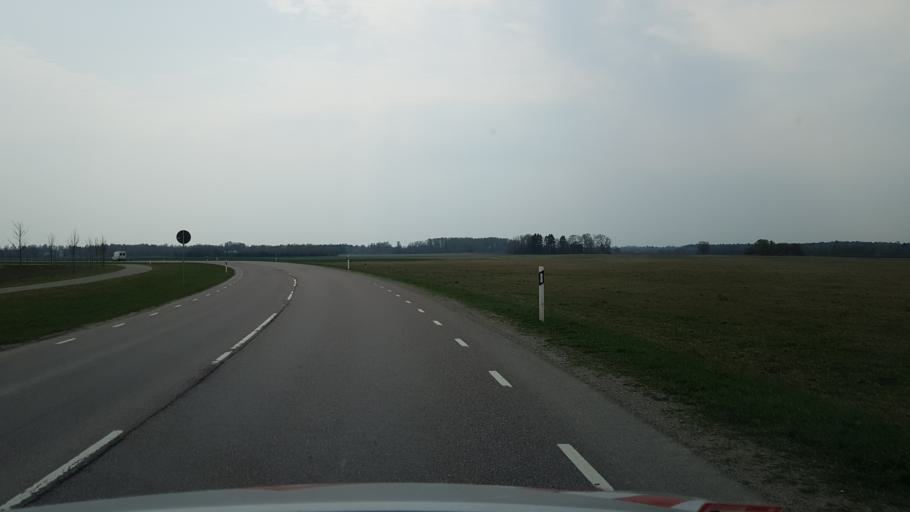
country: EE
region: Harju
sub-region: Kiili vald
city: Kiili
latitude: 59.3214
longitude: 24.8180
